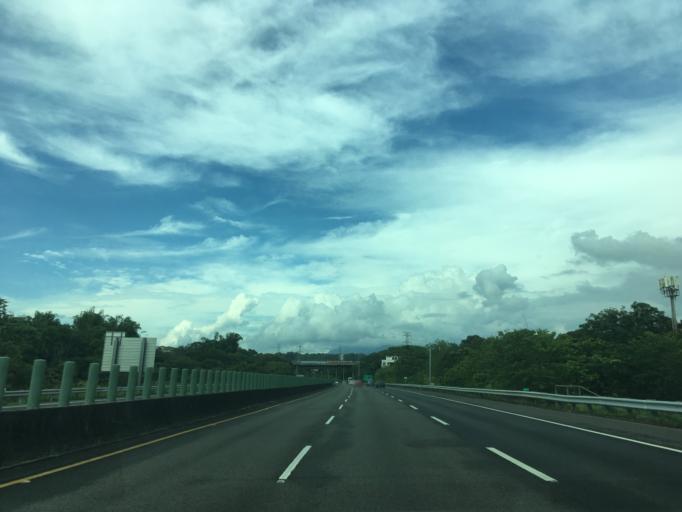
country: TW
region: Taiwan
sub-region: Chiayi
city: Jiayi Shi
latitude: 23.4602
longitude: 120.4933
